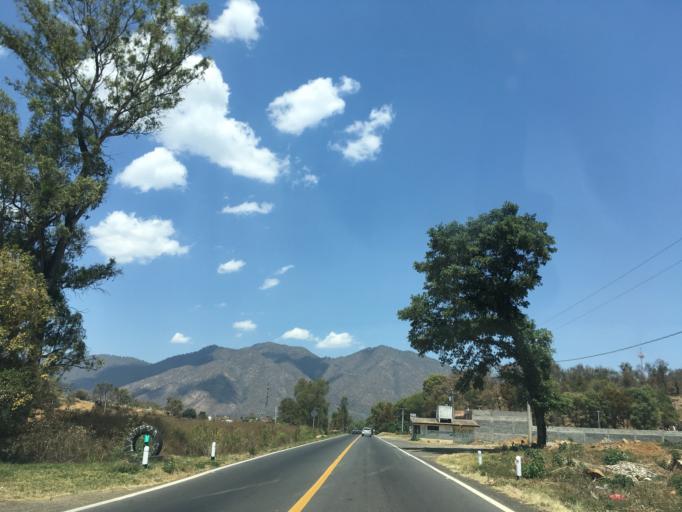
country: MX
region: Michoacan
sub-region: Chilchota
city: Tacuro (Santa Maria Tacuro)
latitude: 19.8448
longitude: -102.0309
